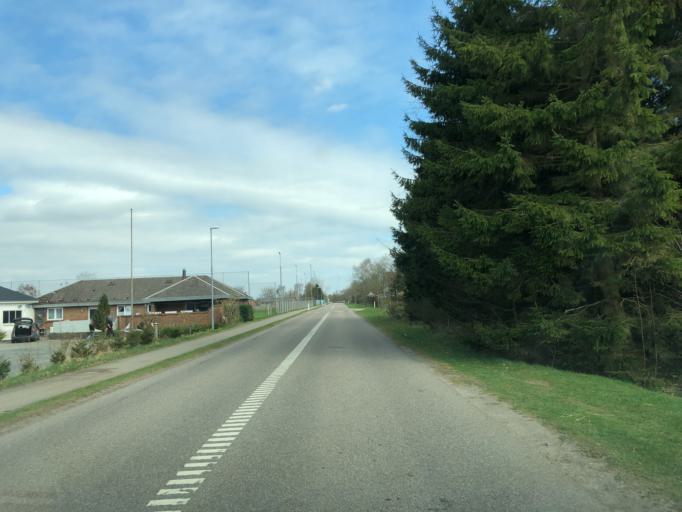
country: DK
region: South Denmark
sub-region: Vejle Kommune
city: Give
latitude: 55.9037
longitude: 9.2636
